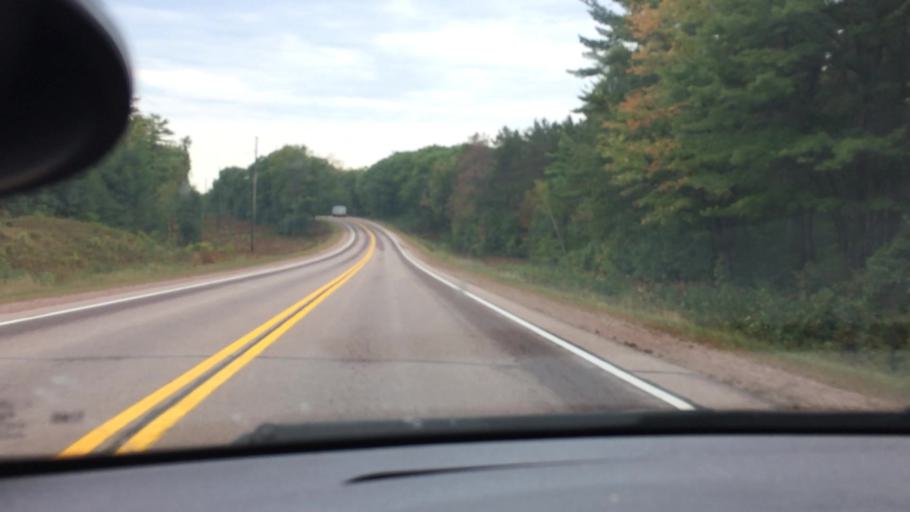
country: US
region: Wisconsin
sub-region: Clark County
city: Neillsville
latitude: 44.5831
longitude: -90.7441
